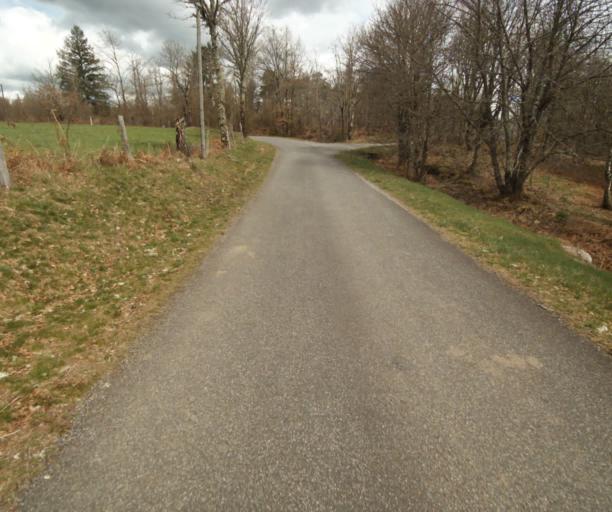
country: FR
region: Limousin
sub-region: Departement de la Correze
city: Correze
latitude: 45.3463
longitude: 1.9388
